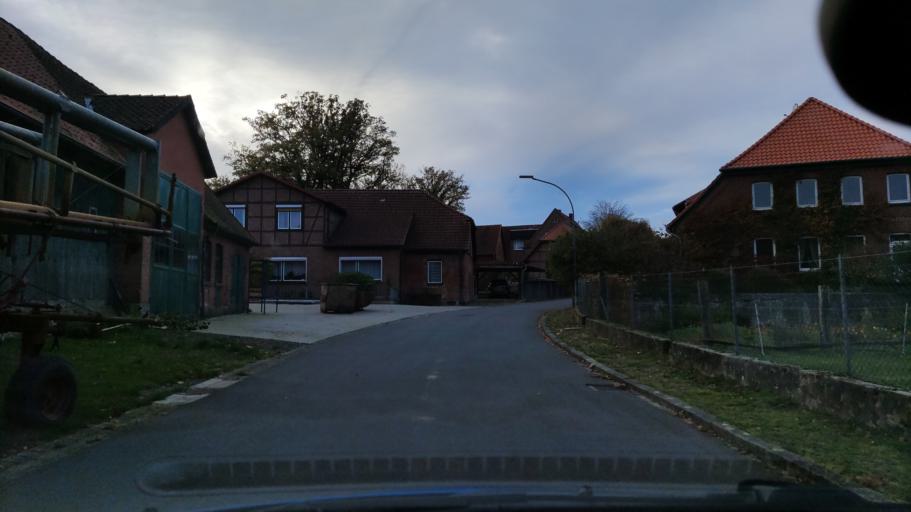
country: DE
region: Lower Saxony
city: Gerdau
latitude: 52.9636
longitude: 10.4577
